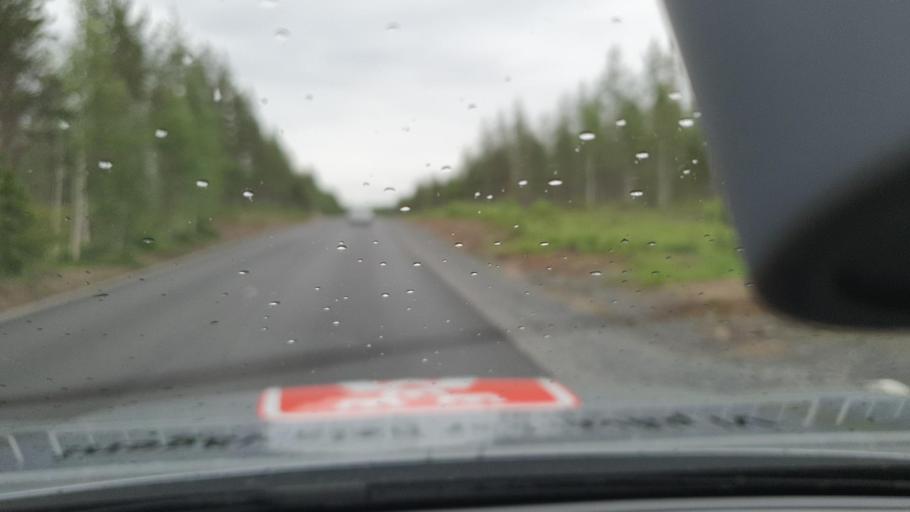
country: SE
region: Norrbotten
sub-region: Overkalix Kommun
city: OEverkalix
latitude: 66.6939
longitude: 23.2037
